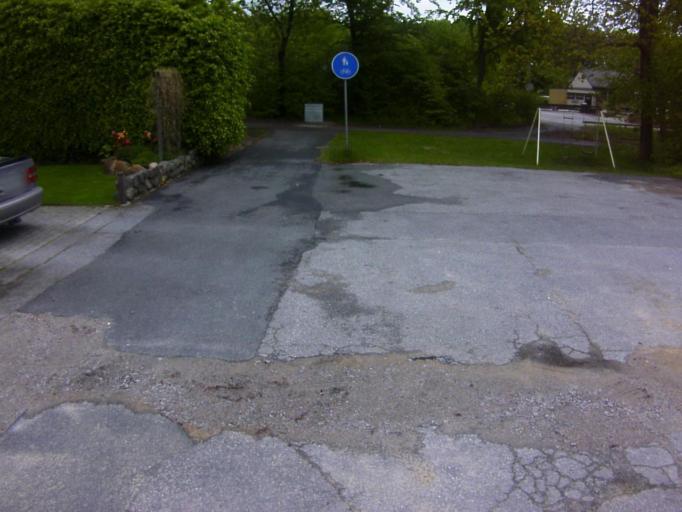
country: SE
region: Blekinge
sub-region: Solvesborgs Kommun
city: Soelvesborg
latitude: 56.0612
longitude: 14.5877
